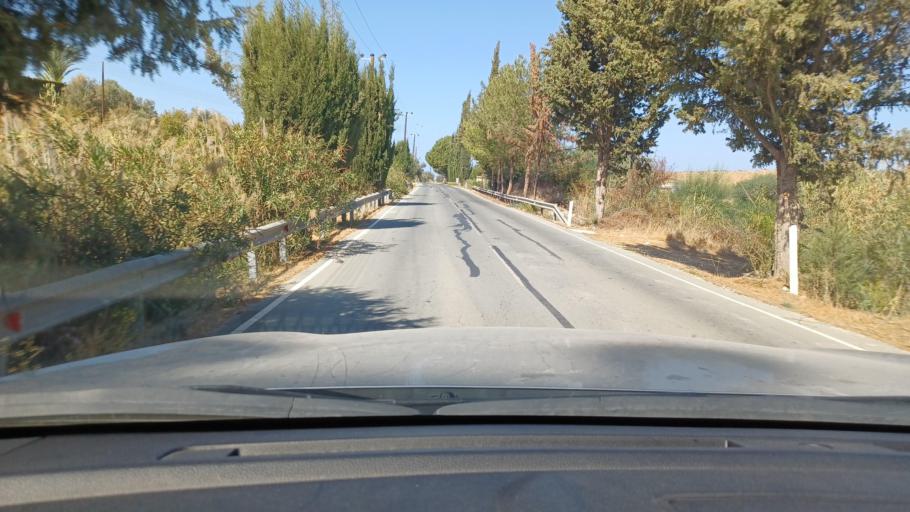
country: CY
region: Pafos
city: Polis
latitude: 35.0190
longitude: 32.4474
